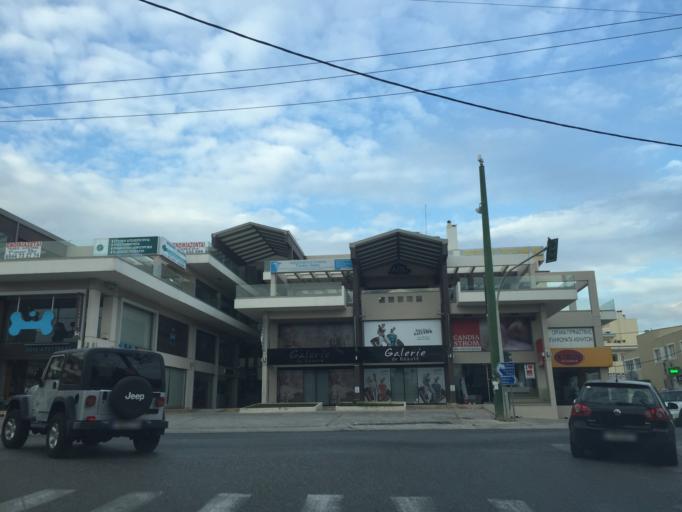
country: GR
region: Attica
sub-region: Nomarchia Anatolikis Attikis
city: Vari
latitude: 37.8332
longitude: 23.8029
